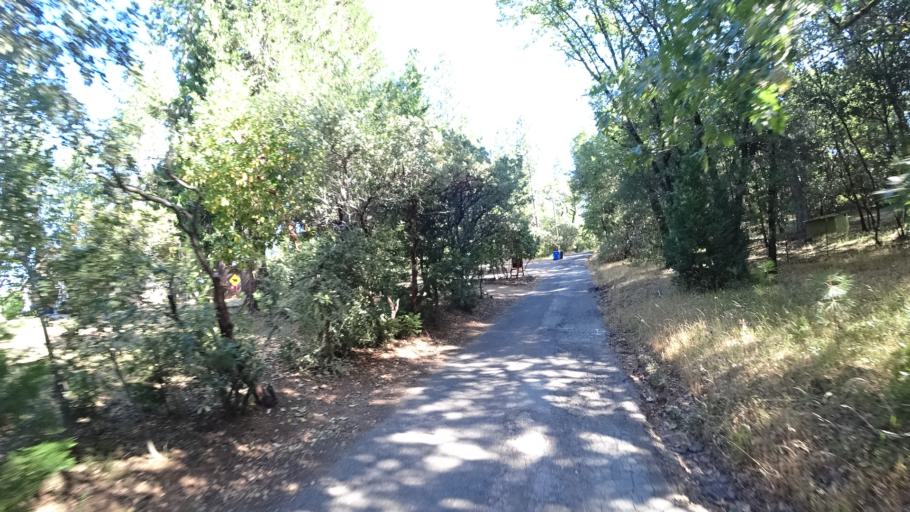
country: US
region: California
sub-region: Amador County
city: Pioneer
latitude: 38.4054
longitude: -120.5588
